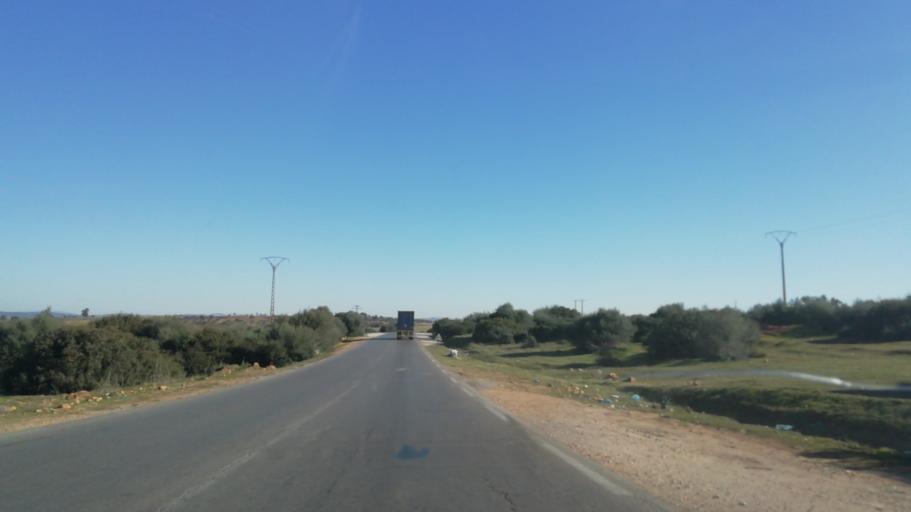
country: DZ
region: Relizane
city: Smala
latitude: 35.6908
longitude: 0.7916
